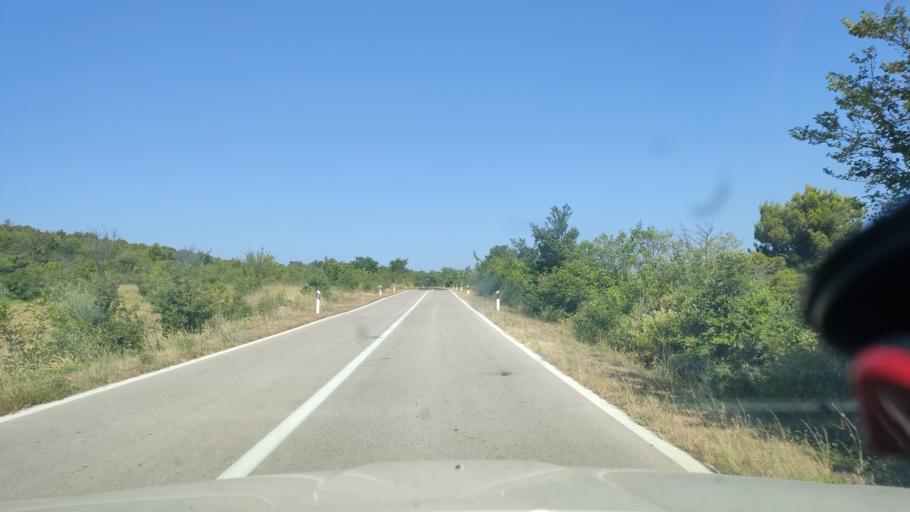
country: HR
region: Sibensko-Kniniska
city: Zaton
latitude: 43.9152
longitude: 15.8333
